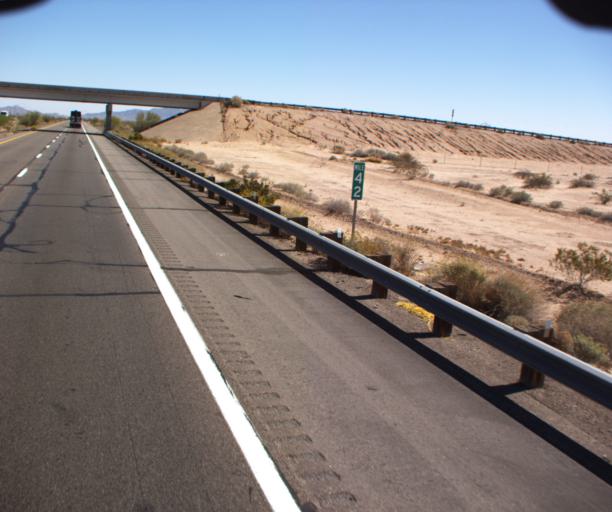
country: US
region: Arizona
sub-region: Yuma County
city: Wellton
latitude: 32.6932
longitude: -113.9543
